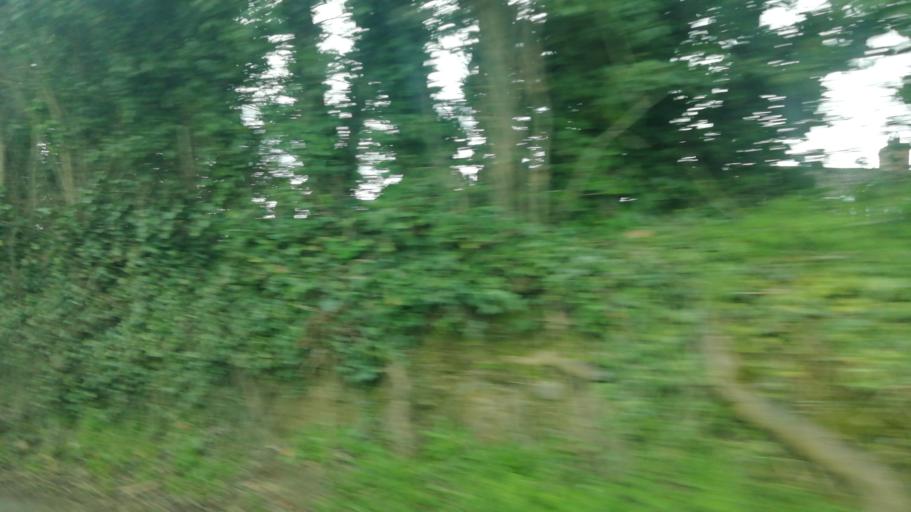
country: IE
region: Leinster
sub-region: Kildare
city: Clane
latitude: 53.2980
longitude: -6.6971
